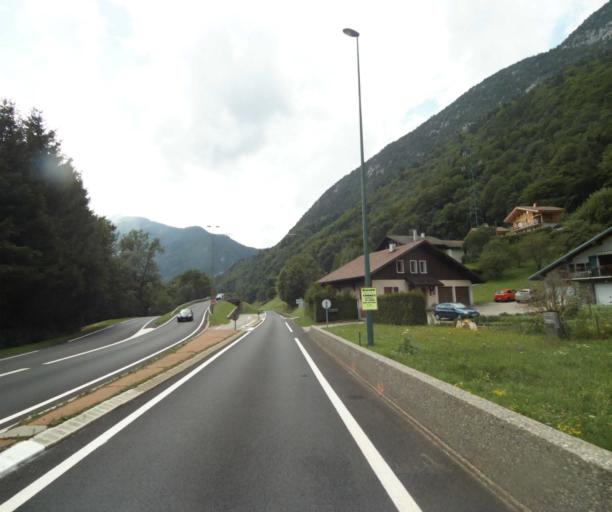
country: FR
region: Rhone-Alpes
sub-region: Departement de la Haute-Savoie
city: Thones
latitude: 45.8920
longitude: 6.3340
